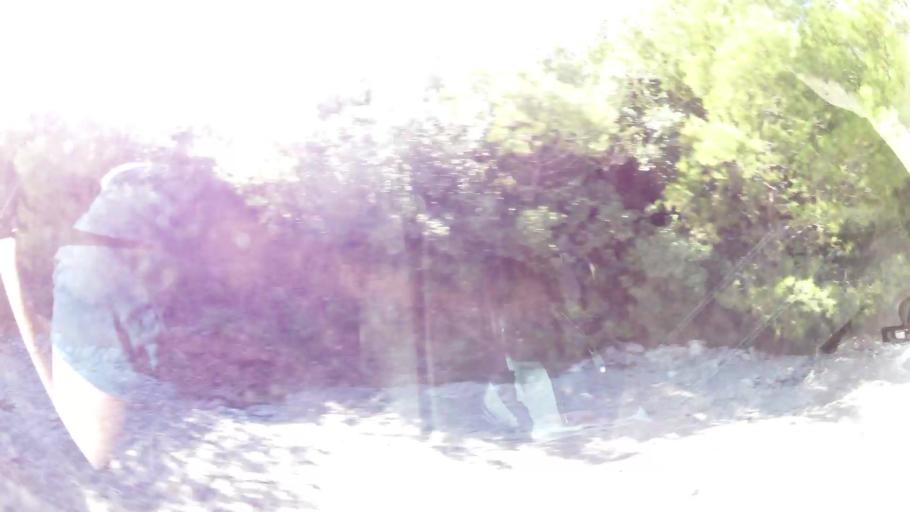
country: GR
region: Attica
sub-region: Nomarchia Anatolikis Attikis
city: Dioni
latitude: 38.0356
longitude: 23.9422
